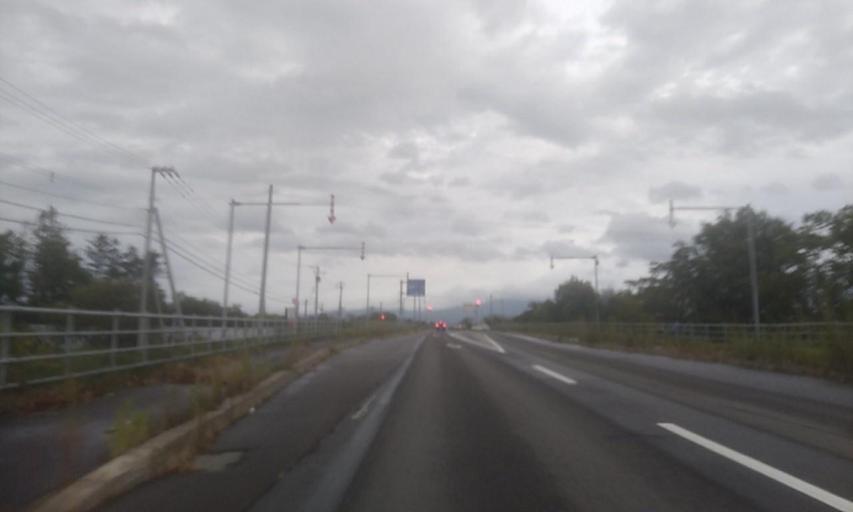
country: JP
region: Hokkaido
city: Abashiri
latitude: 43.8996
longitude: 144.6374
